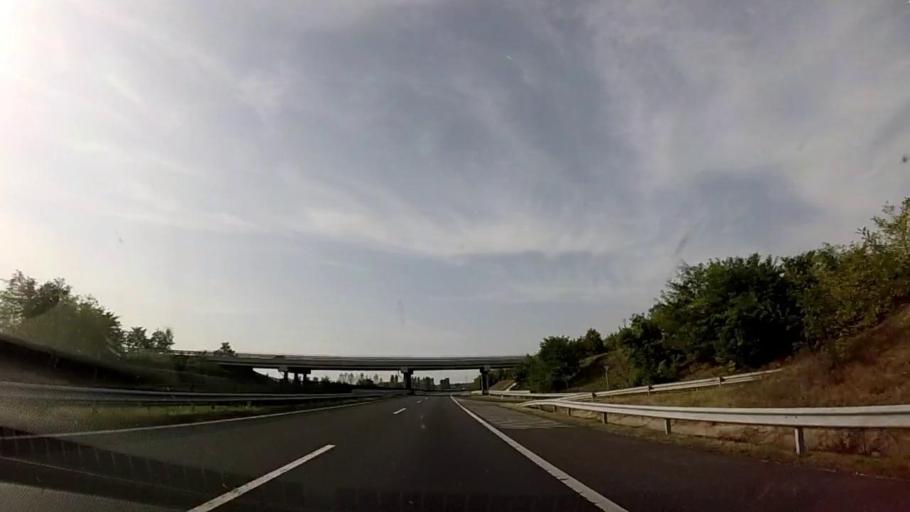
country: HU
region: Somogy
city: Balatonbereny
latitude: 46.6711
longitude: 17.3499
